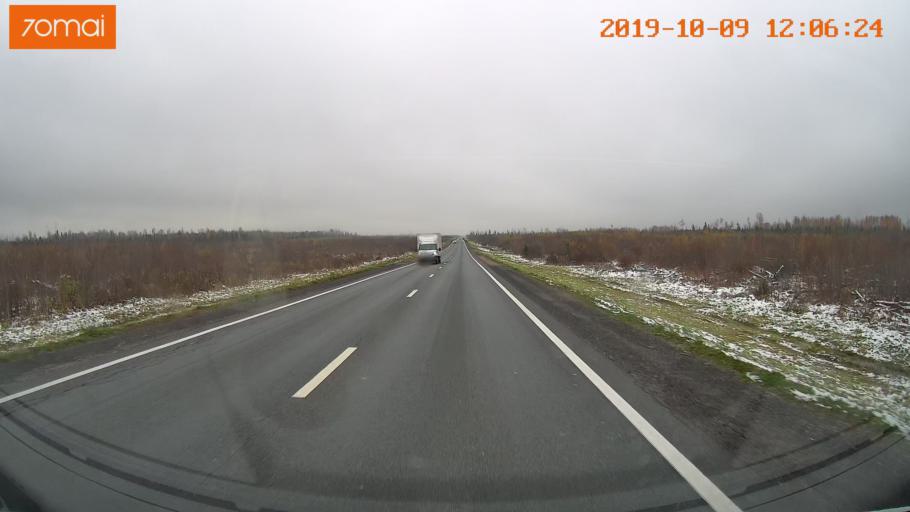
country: RU
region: Jaroslavl
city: Prechistoye
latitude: 58.6150
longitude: 40.3349
